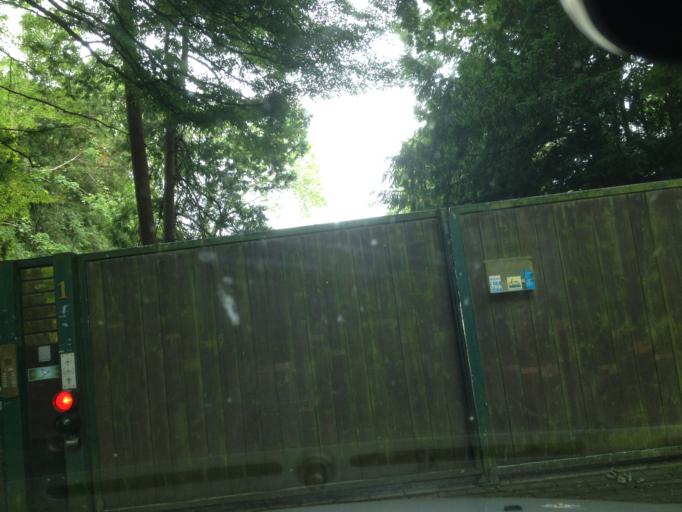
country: DE
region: North Rhine-Westphalia
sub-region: Regierungsbezirk Munster
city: Gelsenkirchen
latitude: 51.4313
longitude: 7.1119
